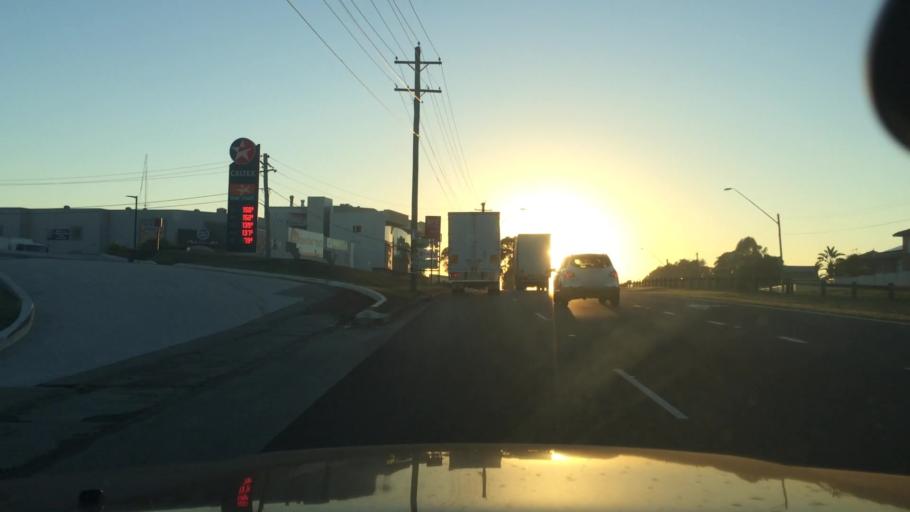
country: AU
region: New South Wales
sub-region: Fairfield
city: Horsley Park
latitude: -33.8526
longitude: 150.8904
